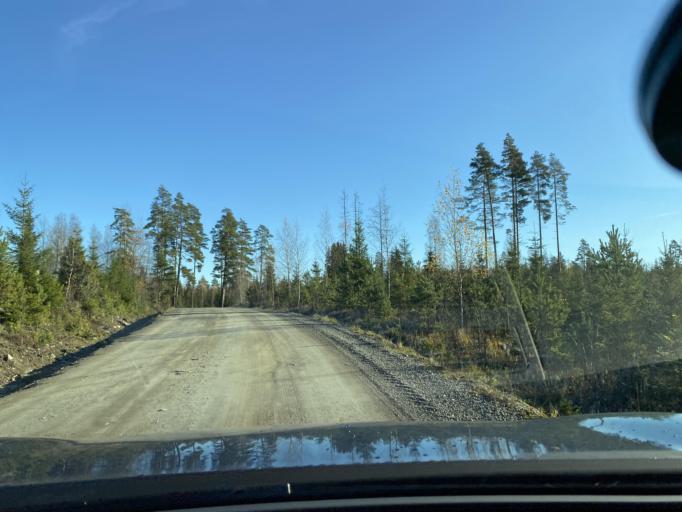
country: FI
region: Haeme
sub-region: Haemeenlinna
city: Kalvola
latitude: 60.9916
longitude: 24.0271
